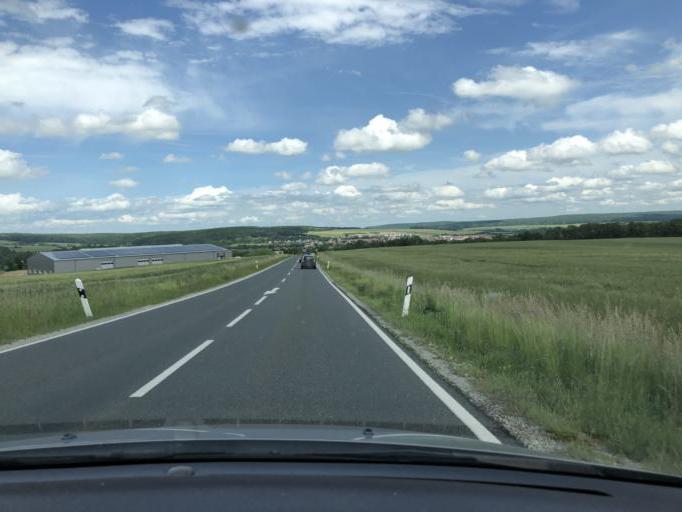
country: DE
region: Thuringia
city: Kefferhausen
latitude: 51.3049
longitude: 10.2936
